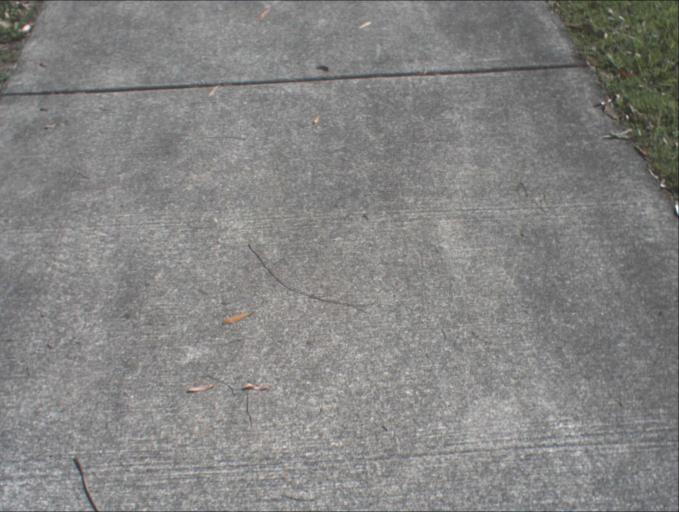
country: AU
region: Queensland
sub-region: Logan
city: Windaroo
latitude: -27.7223
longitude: 153.1737
